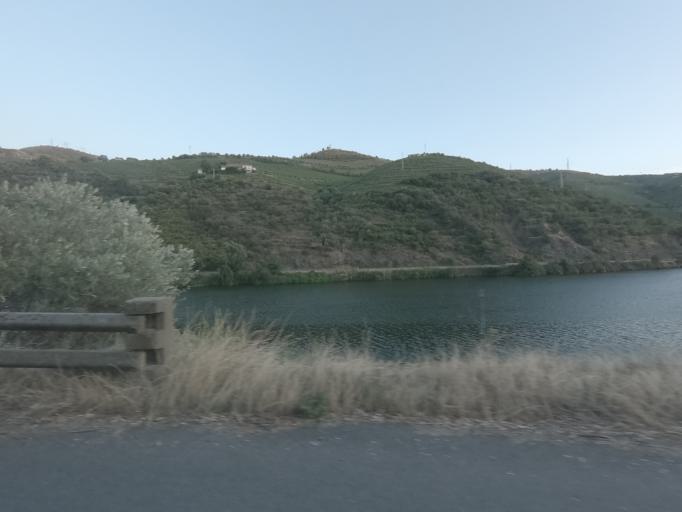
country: PT
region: Viseu
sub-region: Armamar
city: Armamar
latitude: 41.1461
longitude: -7.7290
